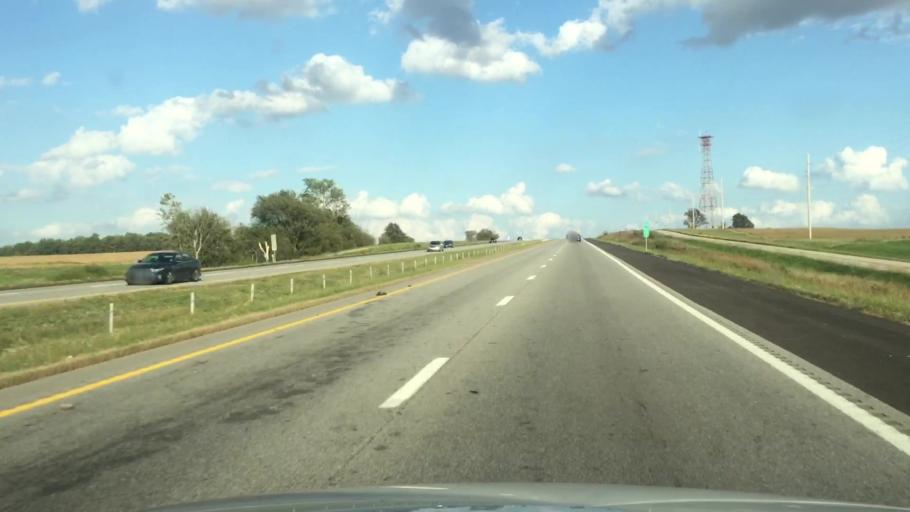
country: US
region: Missouri
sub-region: Lafayette County
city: Higginsville
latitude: 38.9925
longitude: -93.6904
